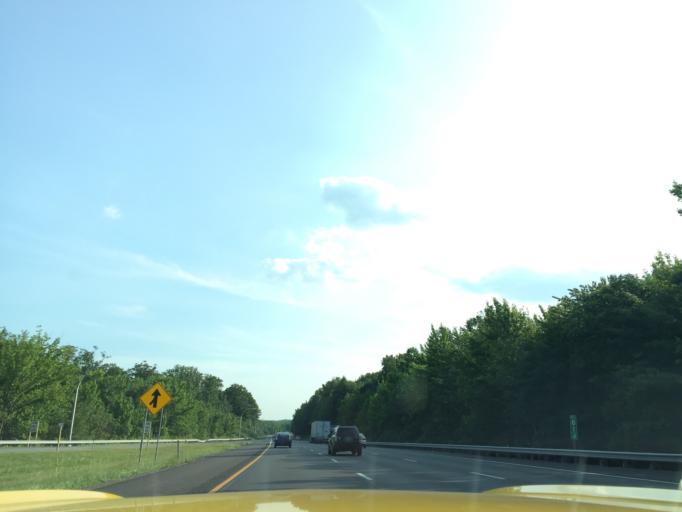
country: US
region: Maryland
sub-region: Harford County
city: Riverside
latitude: 39.4959
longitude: -76.2357
